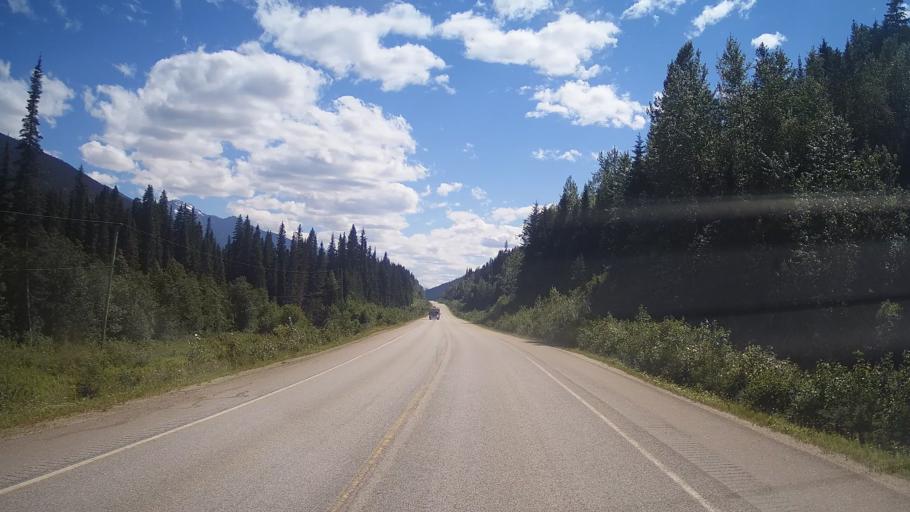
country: CA
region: Alberta
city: Jasper Park Lodge
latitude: 52.5617
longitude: -119.1091
